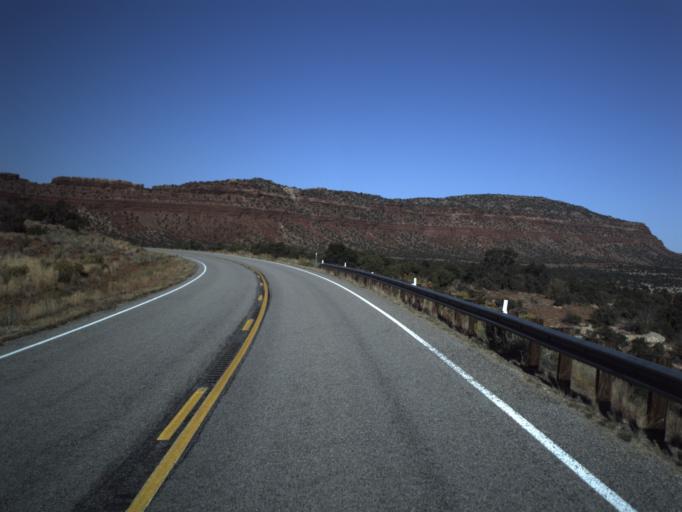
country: US
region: Utah
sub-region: San Juan County
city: Blanding
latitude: 37.6045
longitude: -110.0643
